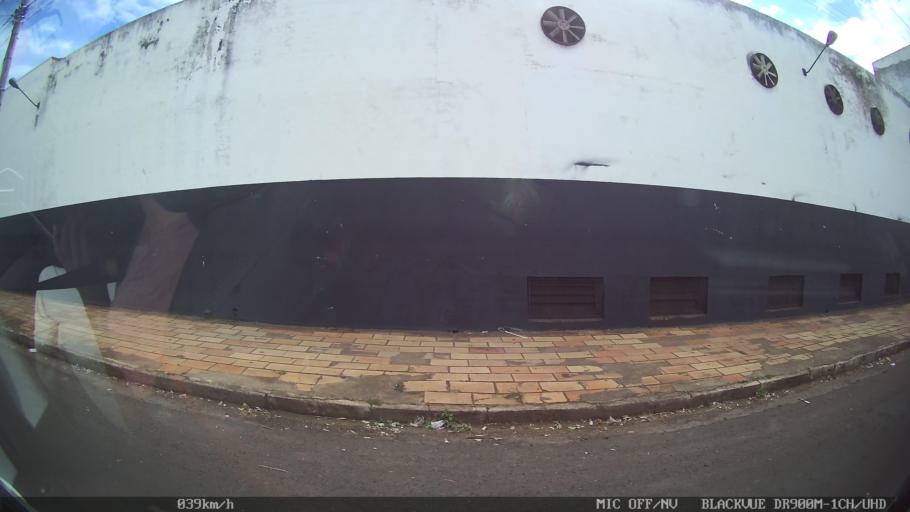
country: BR
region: Sao Paulo
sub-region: Bady Bassitt
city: Bady Bassitt
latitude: -20.8147
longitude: -49.5164
